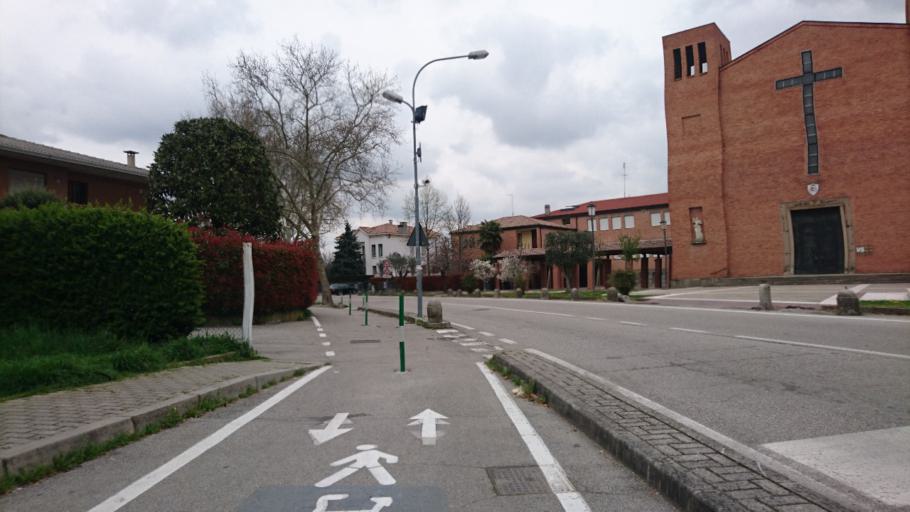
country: IT
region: Veneto
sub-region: Provincia di Padova
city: Vigodarzere
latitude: 45.4471
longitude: 11.8720
